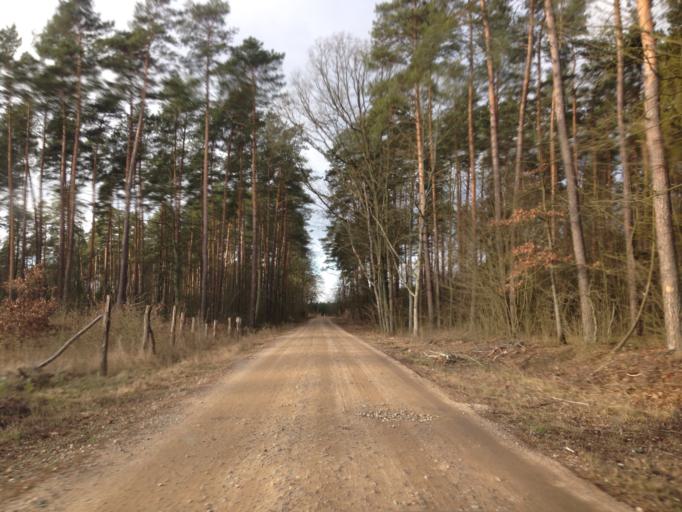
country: PL
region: Kujawsko-Pomorskie
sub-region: Powiat brodnicki
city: Gorzno
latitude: 53.2287
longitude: 19.6597
